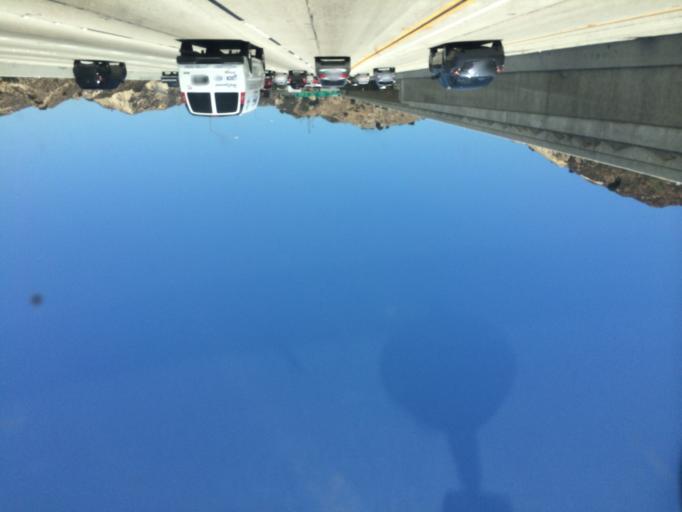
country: US
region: California
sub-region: Los Angeles County
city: Santa Clarita
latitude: 34.3285
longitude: -118.5051
